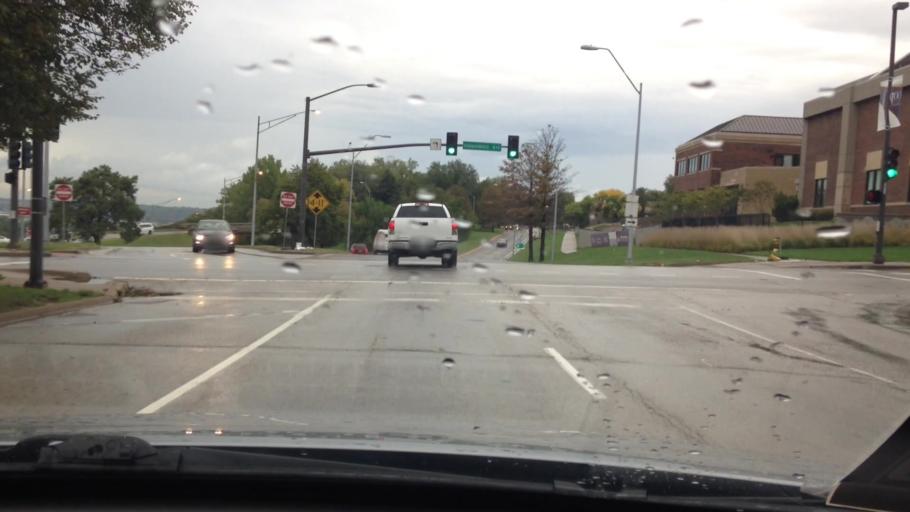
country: US
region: Missouri
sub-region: Jackson County
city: Kansas City
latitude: 39.1065
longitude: -94.5635
